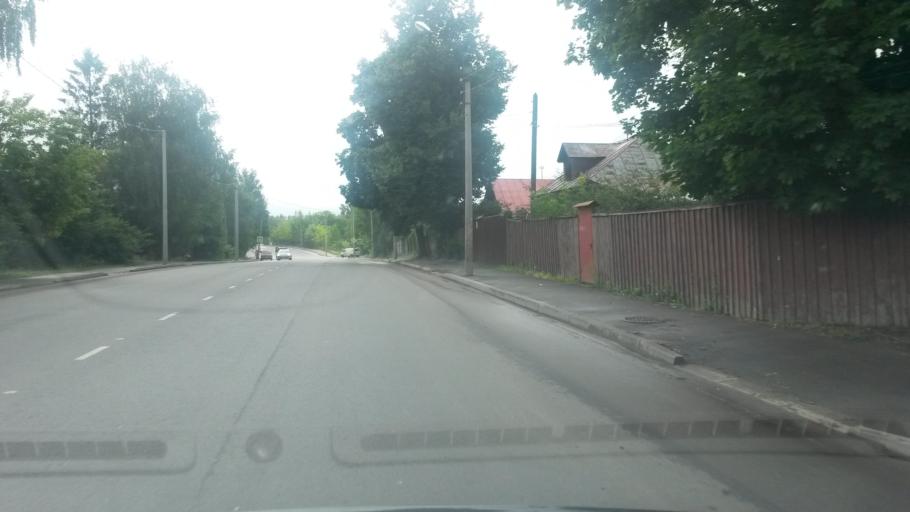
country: RU
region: Ivanovo
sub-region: Gorod Ivanovo
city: Ivanovo
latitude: 57.0194
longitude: 40.9224
